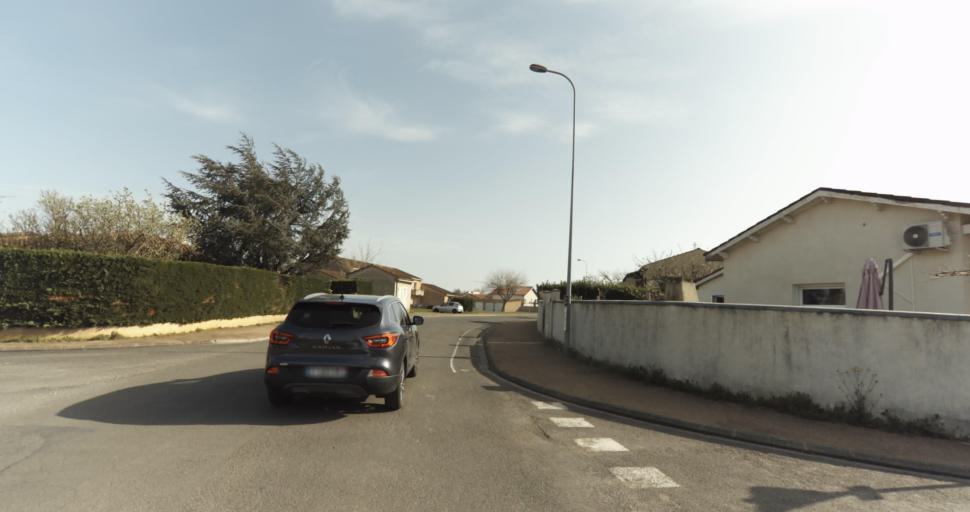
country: FR
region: Midi-Pyrenees
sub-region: Departement du Tarn
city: Saint-Sulpice-la-Pointe
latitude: 43.7689
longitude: 1.6935
